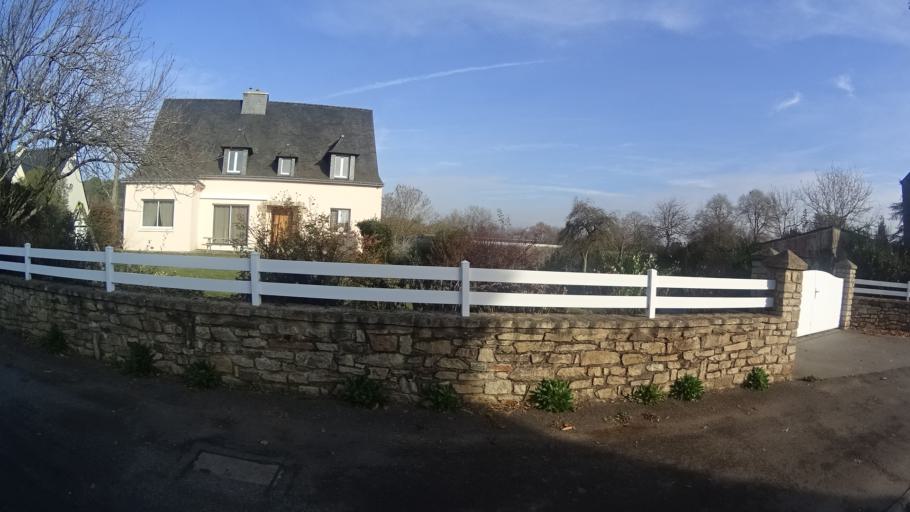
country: FR
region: Brittany
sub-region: Departement du Morbihan
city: Rieux
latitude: 47.5985
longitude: -2.1098
